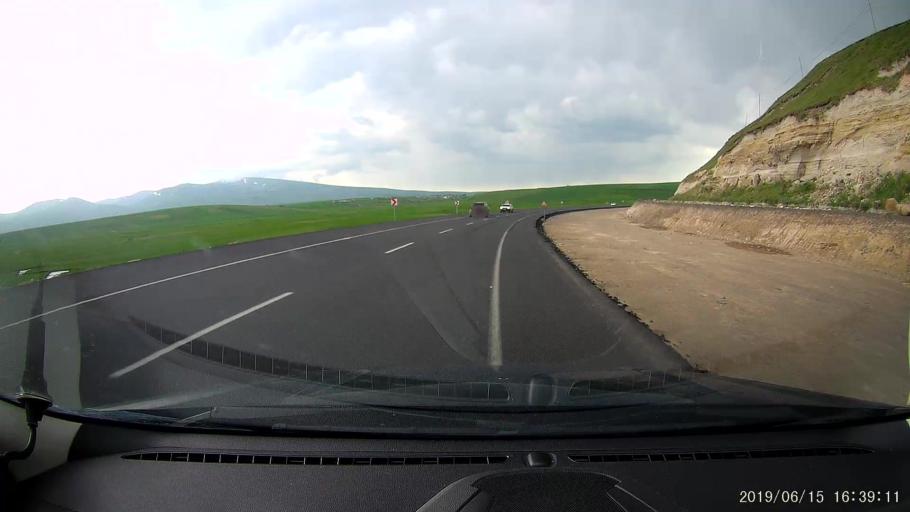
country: TR
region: Ardahan
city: Haskoy
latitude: 40.9856
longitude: 42.8950
